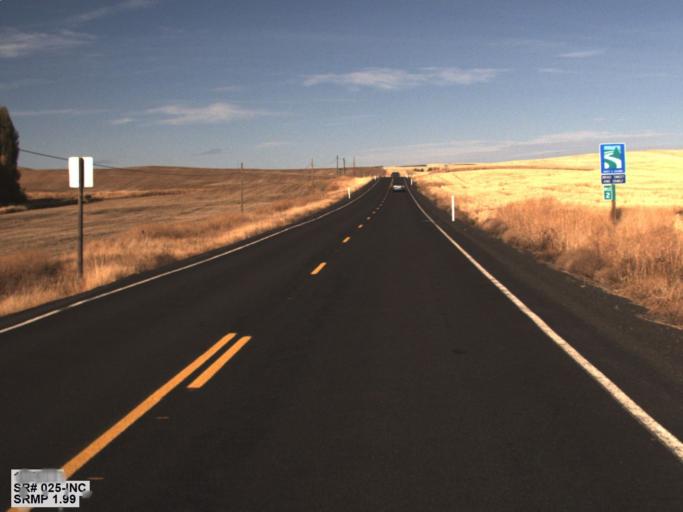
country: US
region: Washington
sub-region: Lincoln County
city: Davenport
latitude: 47.6836
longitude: -118.1410
